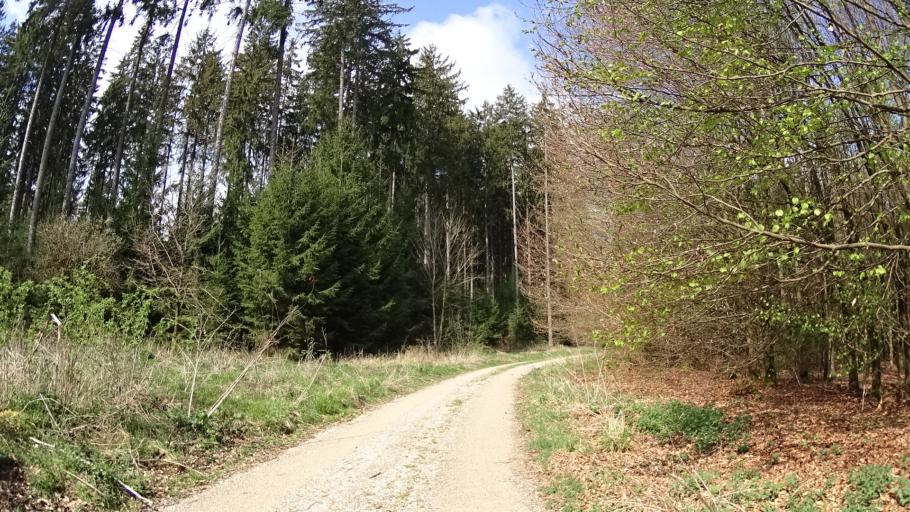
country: DE
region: Bavaria
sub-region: Upper Bavaria
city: Bohmfeld
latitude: 48.8926
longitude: 11.3871
